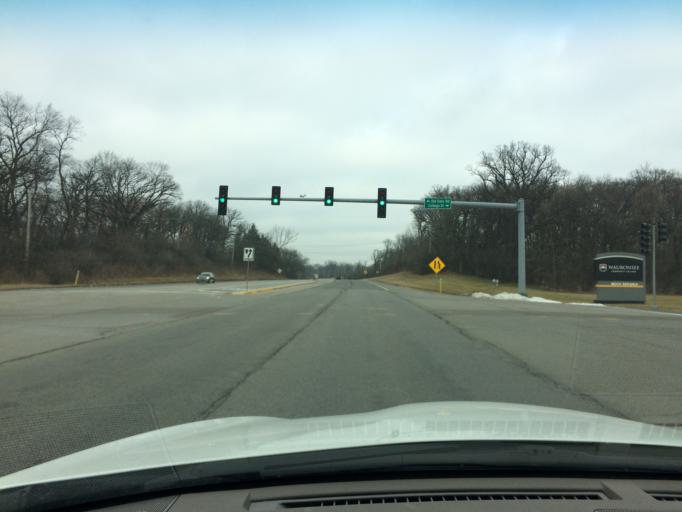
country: US
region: Illinois
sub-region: Kane County
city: Sugar Grove
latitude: 41.8007
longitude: -88.4613
